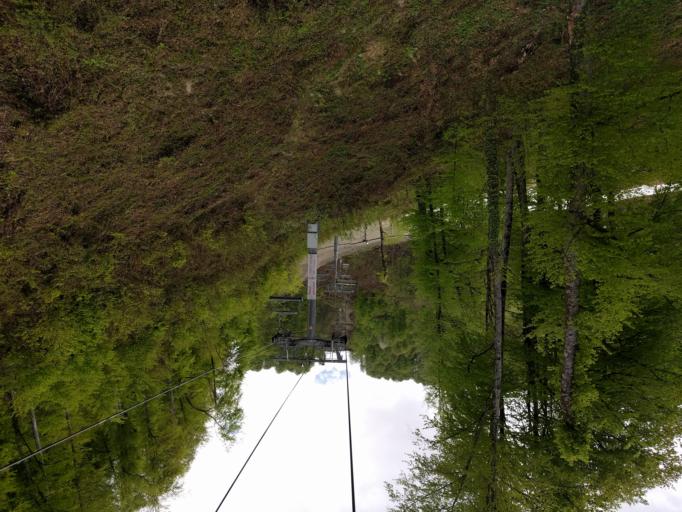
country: RU
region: Krasnodarskiy
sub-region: Sochi City
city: Krasnaya Polyana
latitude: 43.6470
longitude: 40.3300
